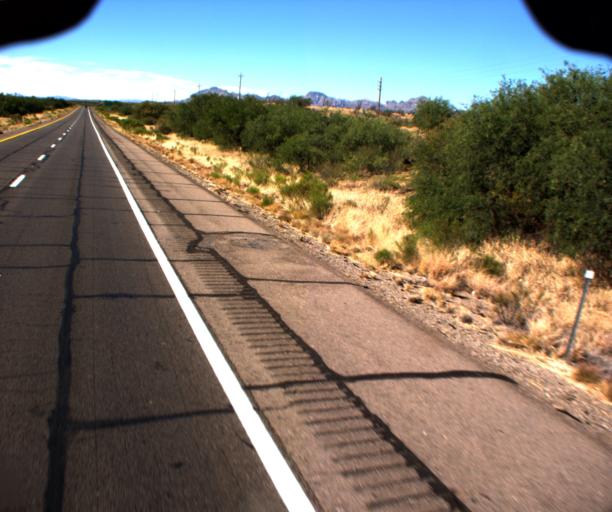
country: US
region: Arizona
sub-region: Pima County
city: Arivaca Junction
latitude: 31.6865
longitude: -111.0648
